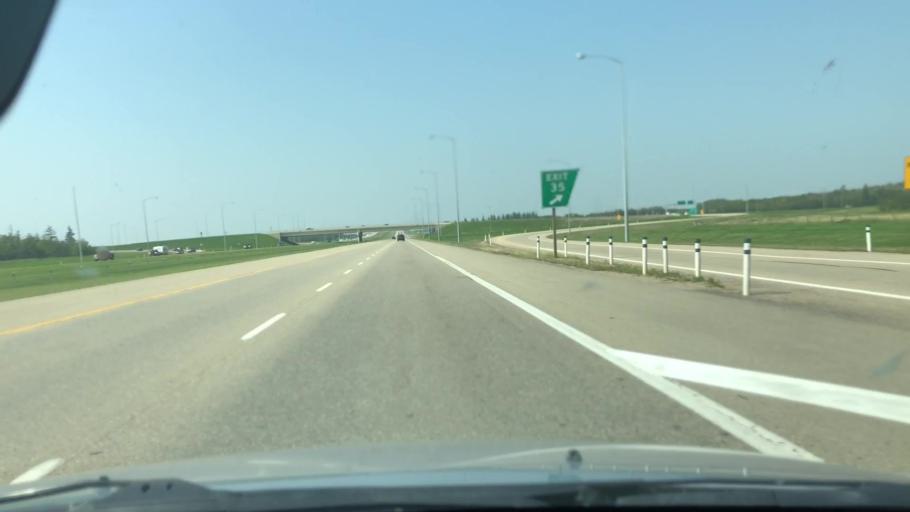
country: CA
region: Alberta
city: St. Albert
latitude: 53.6417
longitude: -113.5376
